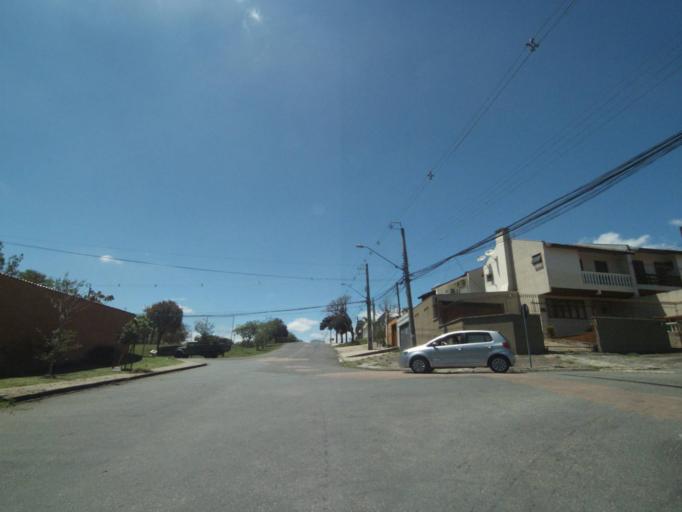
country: BR
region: Parana
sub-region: Curitiba
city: Curitiba
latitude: -25.3945
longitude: -49.2647
